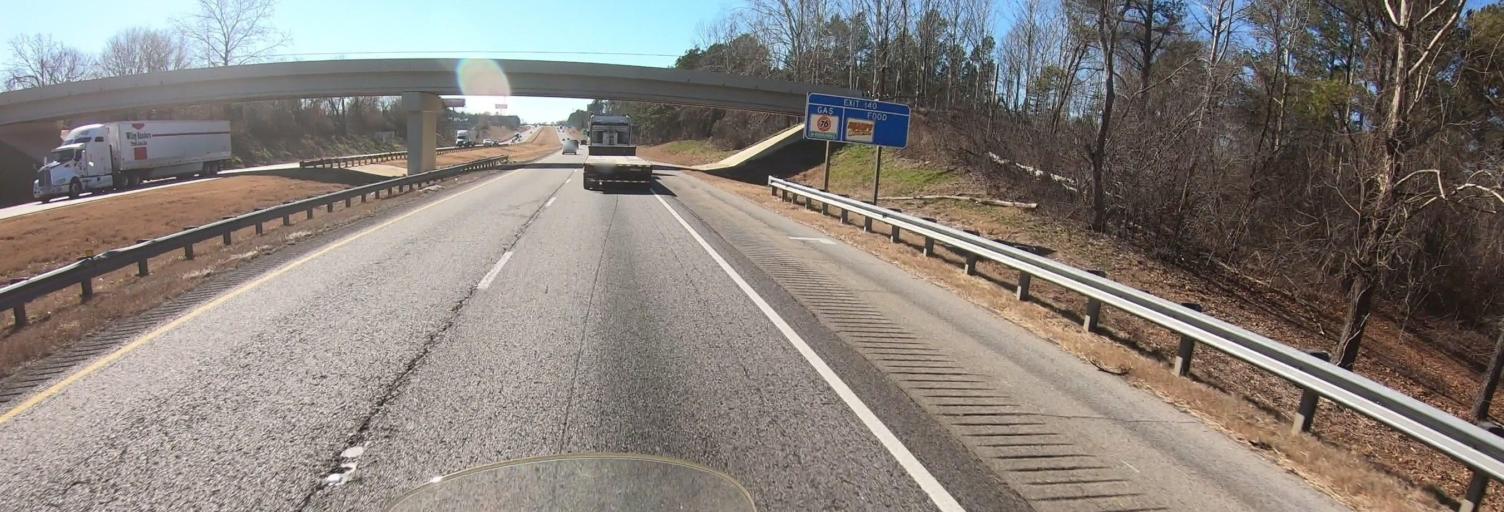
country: US
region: Georgia
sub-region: Banks County
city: Maysville
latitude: 34.1946
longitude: -83.5795
